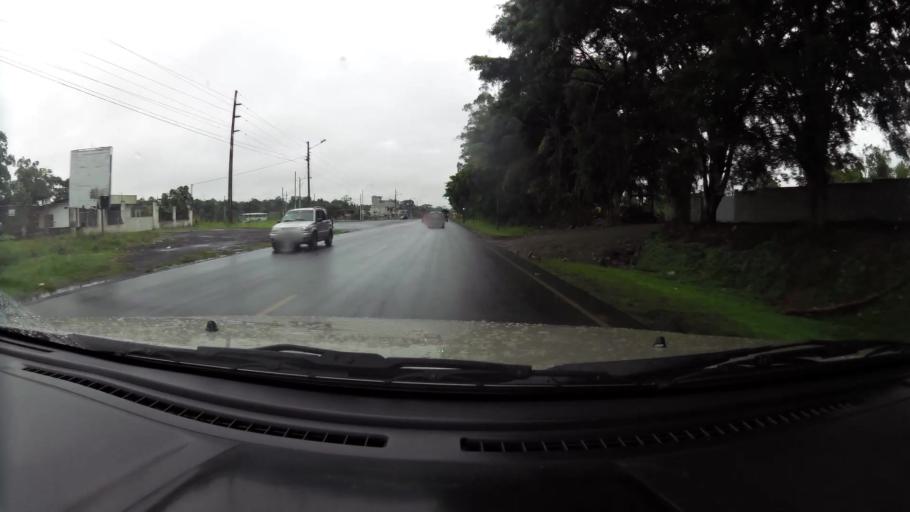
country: EC
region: Santo Domingo de los Tsachilas
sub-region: Canton Santo Domingo de los Colorados
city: Santo Domingo de los Colorados
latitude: -0.2350
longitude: -79.1565
